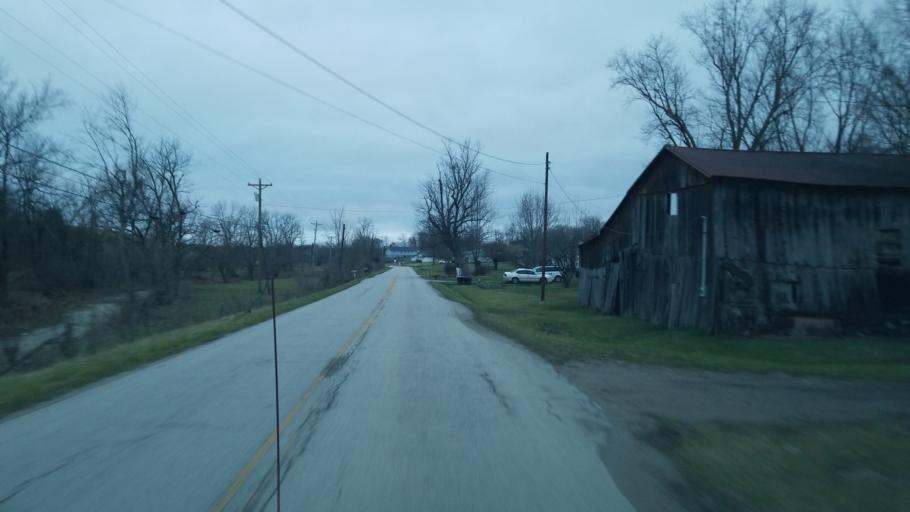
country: US
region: Kentucky
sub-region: Mason County
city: Maysville
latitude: 38.5714
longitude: -83.6927
